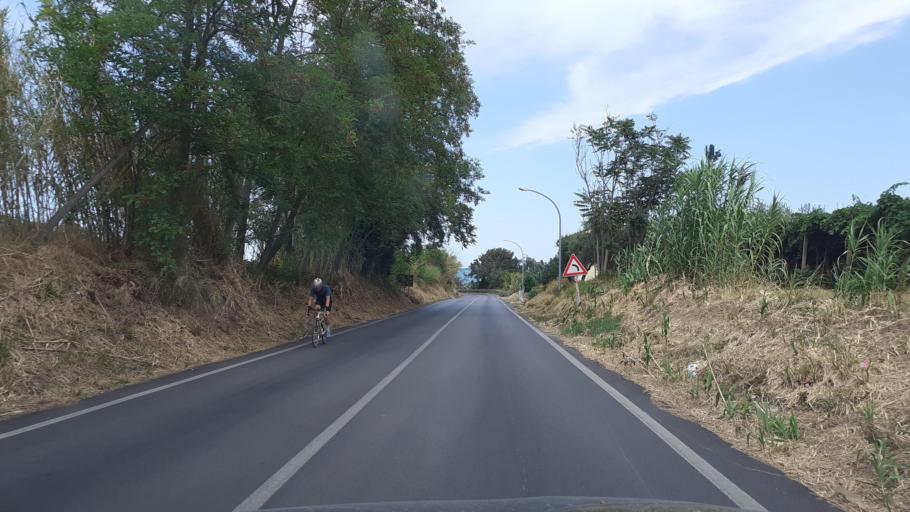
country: IT
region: Abruzzo
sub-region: Provincia di Chieti
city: Fossacesia
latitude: 42.2503
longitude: 14.5046
